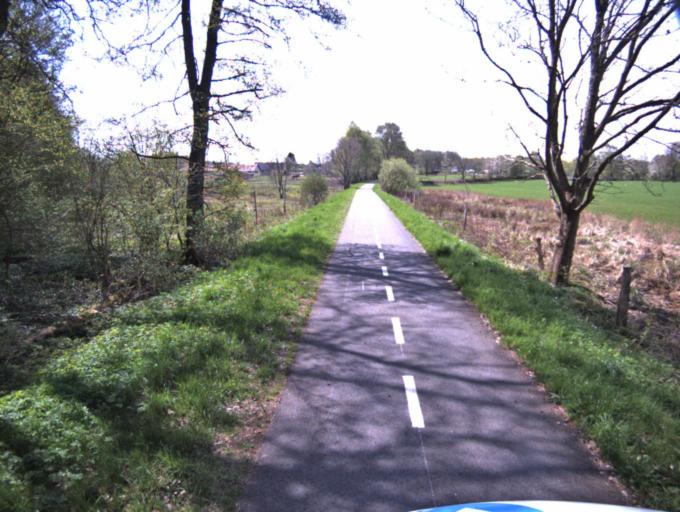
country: SE
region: Skane
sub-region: Kristianstads Kommun
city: Onnestad
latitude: 56.0013
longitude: 14.0450
